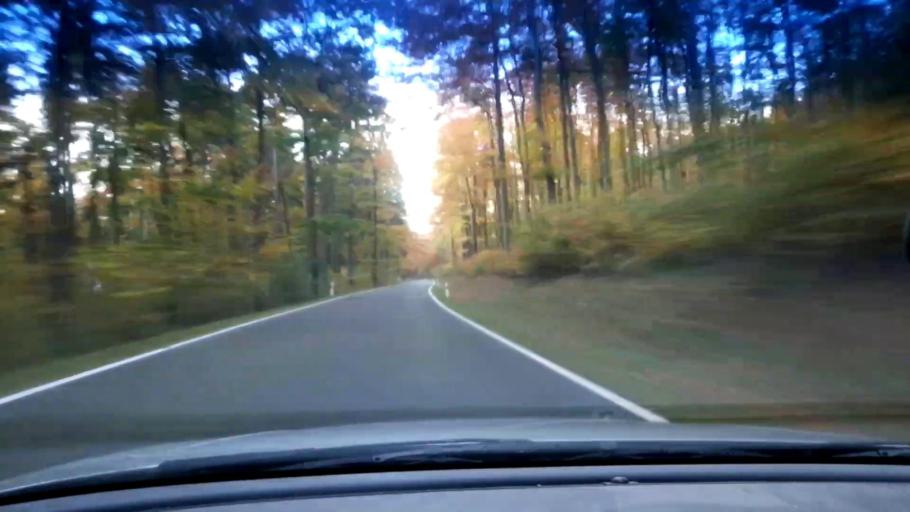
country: DE
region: Bavaria
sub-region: Upper Franconia
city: Heiligenstadt
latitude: 49.8725
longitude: 11.1343
